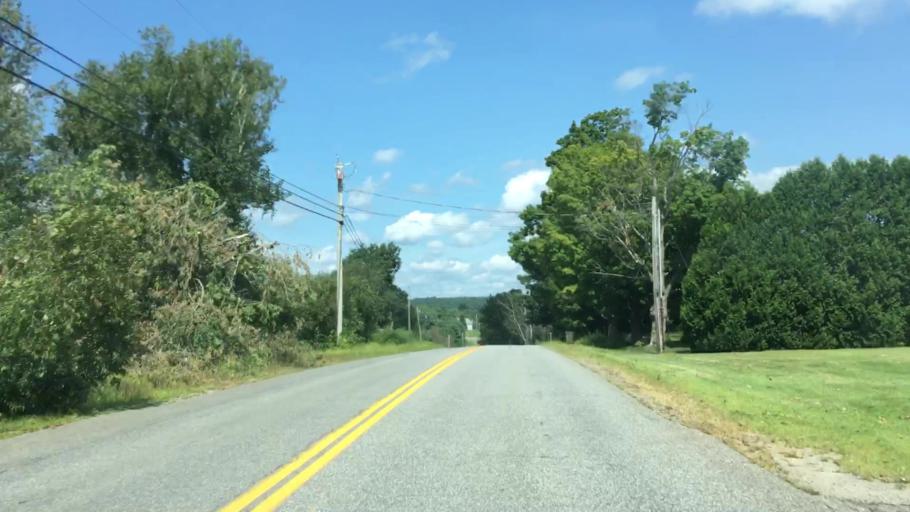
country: US
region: Maine
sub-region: Kennebec County
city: Augusta
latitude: 44.3506
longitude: -69.8132
